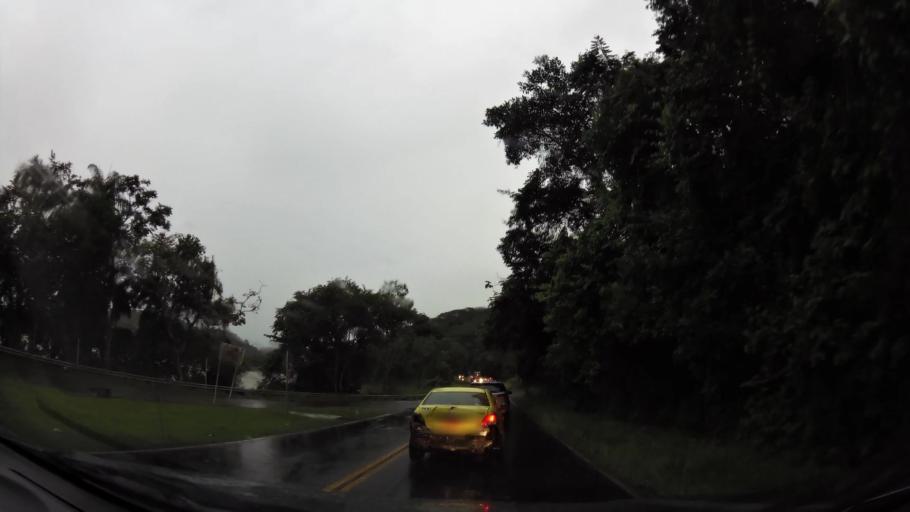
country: PA
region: Panama
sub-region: Distrito de Panama
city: Paraiso
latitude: 9.0108
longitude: -79.5956
